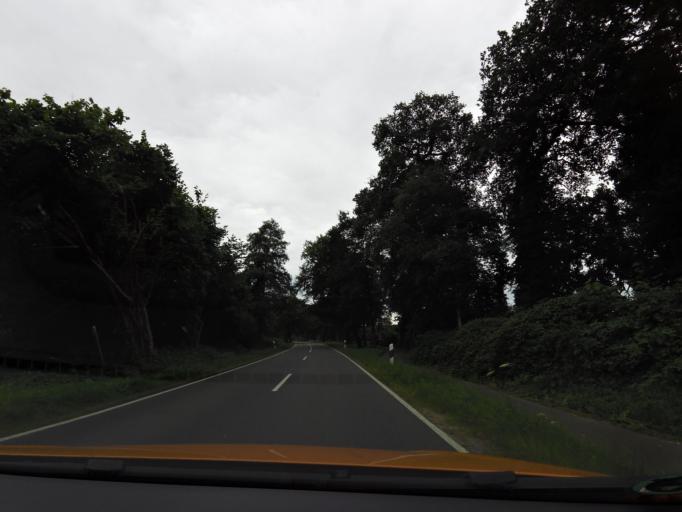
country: DE
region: Lower Saxony
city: Wiefelstede
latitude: 53.2038
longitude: 8.1176
